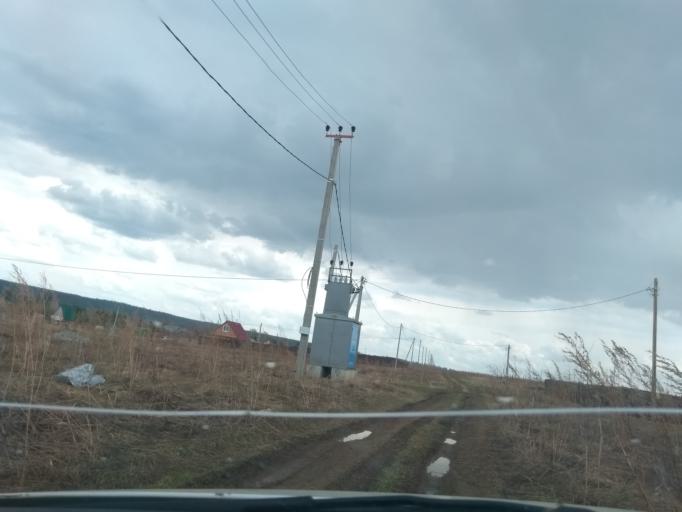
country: RU
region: Perm
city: Sylva
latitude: 57.8458
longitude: 56.7857
